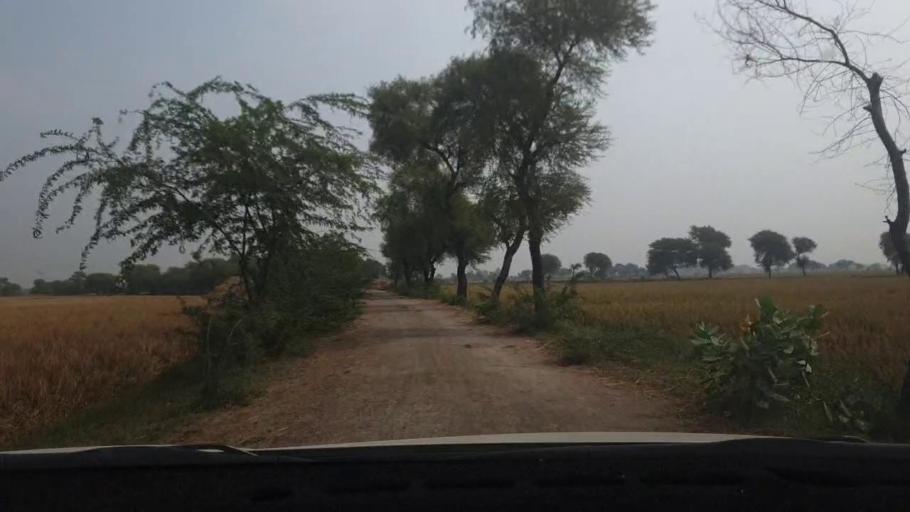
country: PK
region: Sindh
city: Tando Muhammad Khan
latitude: 25.0553
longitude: 68.5300
